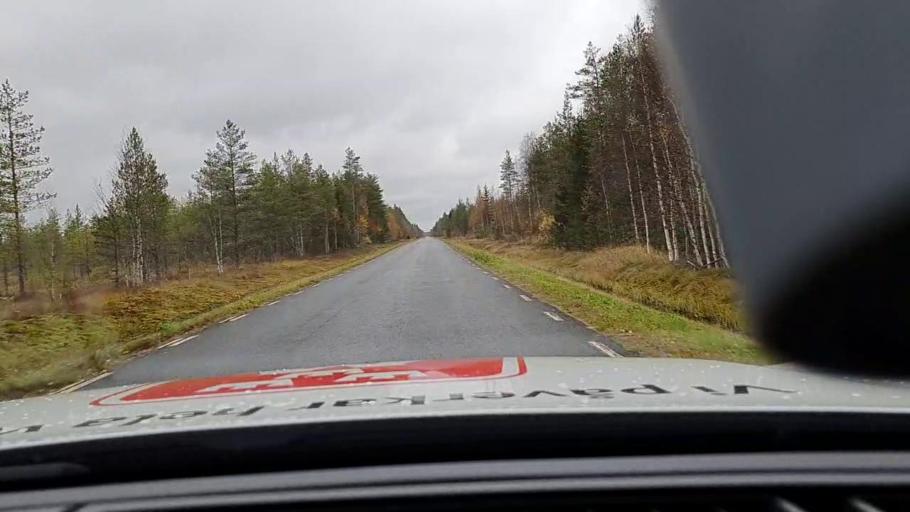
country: SE
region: Norrbotten
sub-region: Haparanda Kommun
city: Haparanda
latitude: 65.9077
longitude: 23.8314
